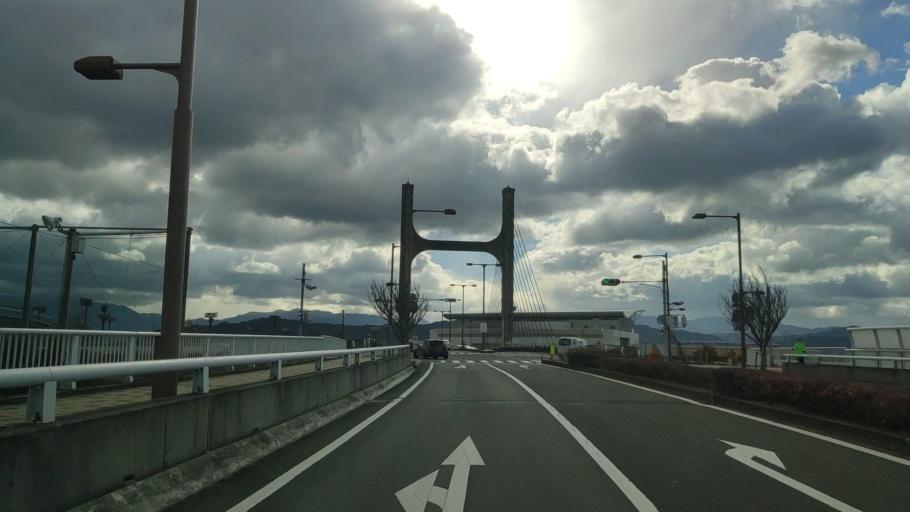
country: JP
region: Ehime
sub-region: Shikoku-chuo Shi
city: Matsuyama
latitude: 33.8116
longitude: 132.7413
